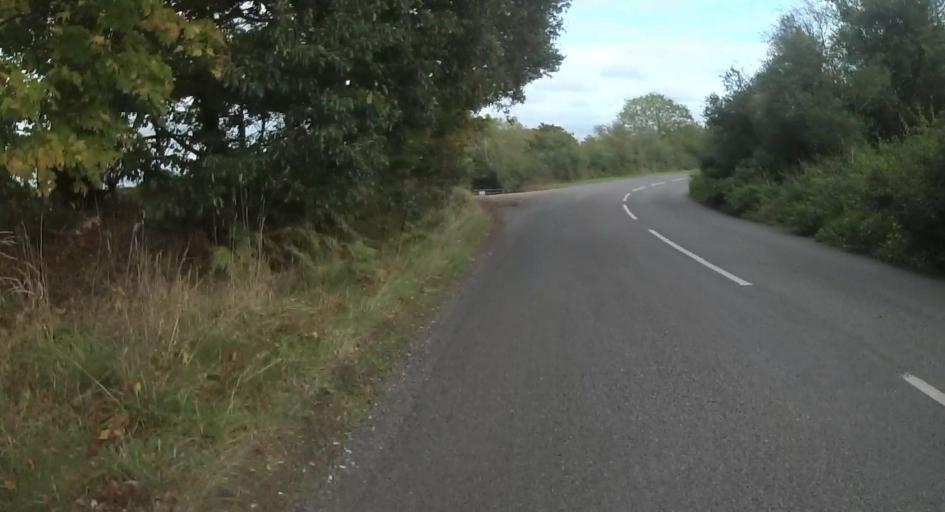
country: GB
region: England
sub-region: Hampshire
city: Odiham
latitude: 51.2918
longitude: -0.8950
